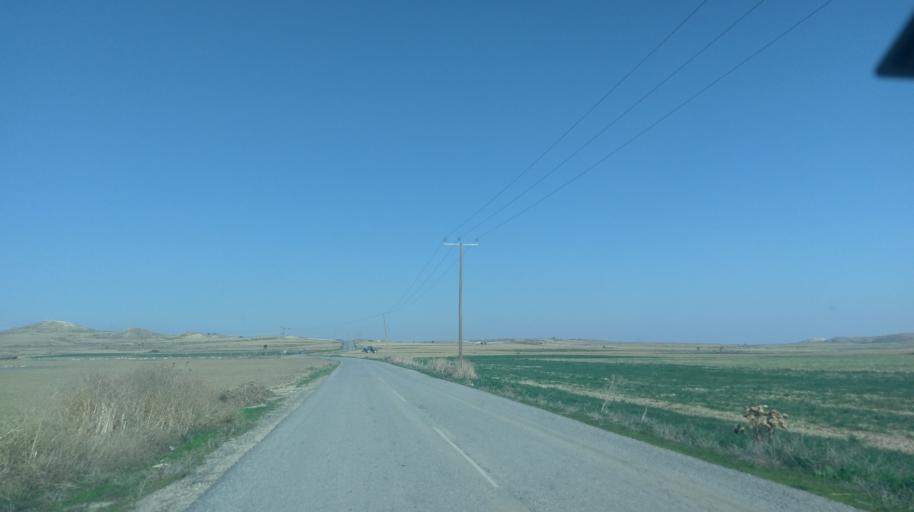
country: CY
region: Lefkosia
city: Lympia
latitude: 35.0377
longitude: 33.4778
